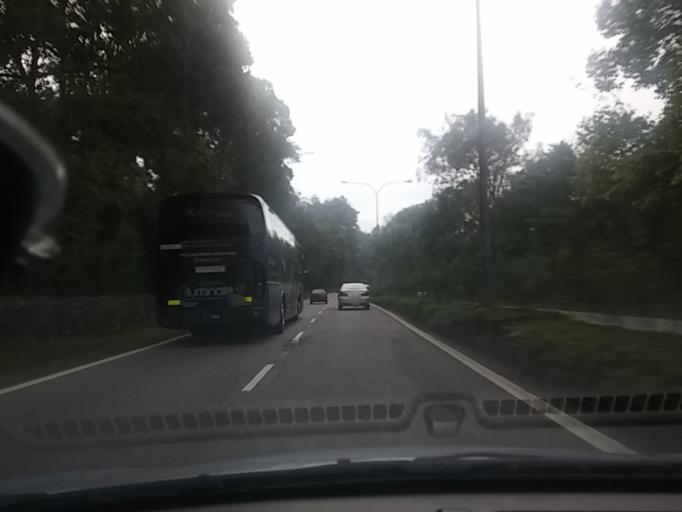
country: MY
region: Pahang
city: Kampung Bukit Tinggi, Bentong
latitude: 3.3906
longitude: 101.7702
